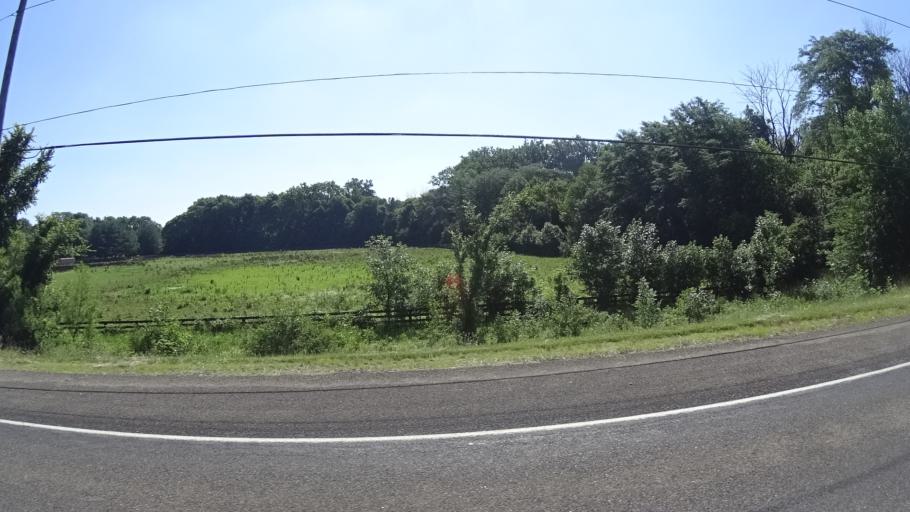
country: US
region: Indiana
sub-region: Hancock County
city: Fortville
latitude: 39.9673
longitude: -85.8432
